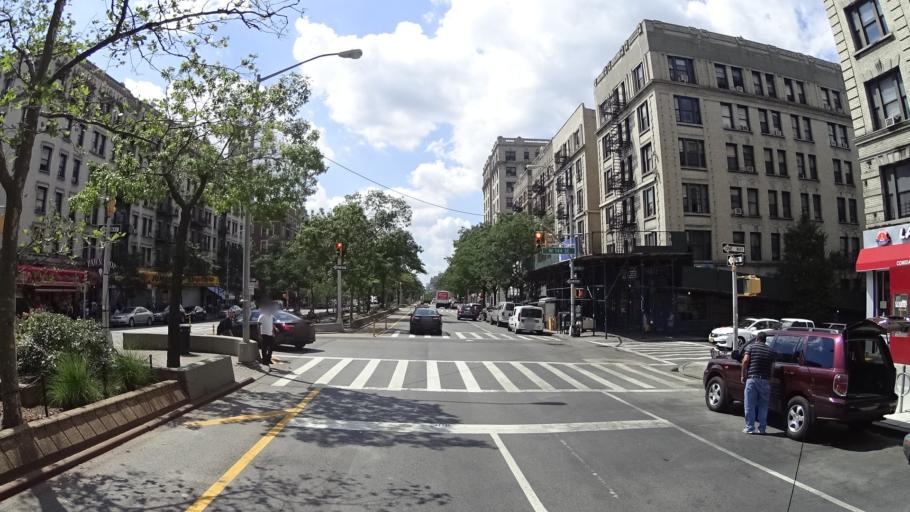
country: US
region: New Jersey
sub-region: Bergen County
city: Edgewater
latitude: 40.8258
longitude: -73.9511
